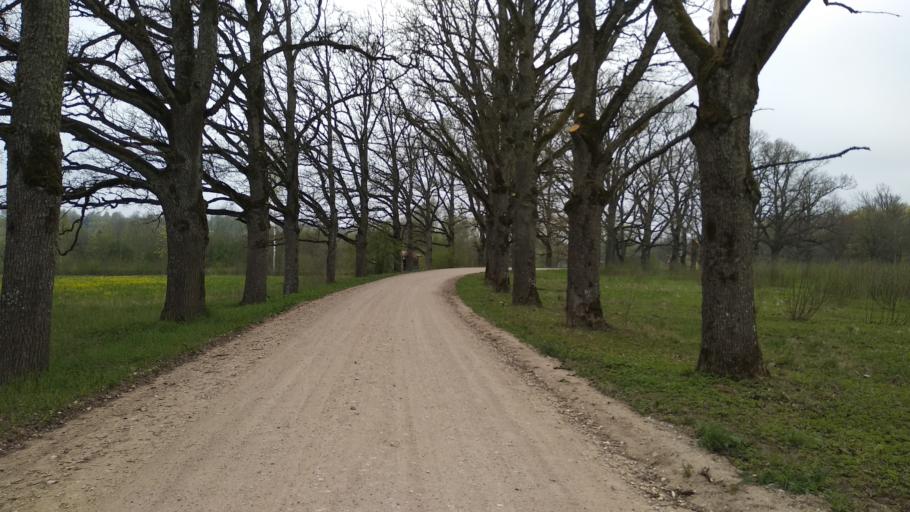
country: LV
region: Malpils
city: Malpils
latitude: 57.0160
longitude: 24.9554
